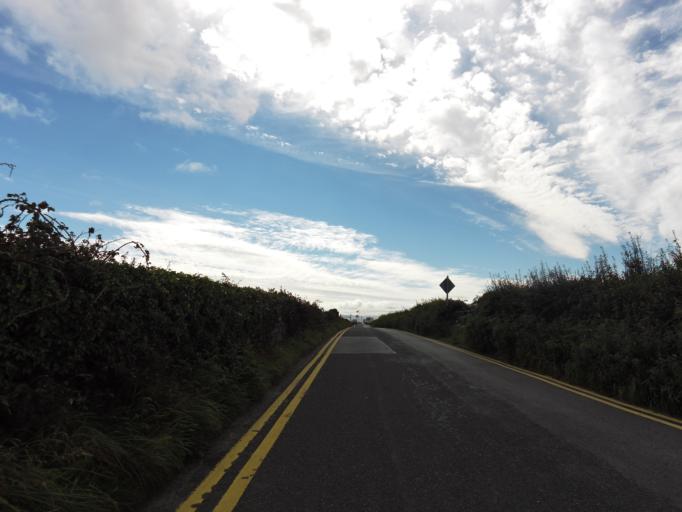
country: IE
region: Connaught
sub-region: County Galway
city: Bearna
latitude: 53.2526
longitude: -9.1289
